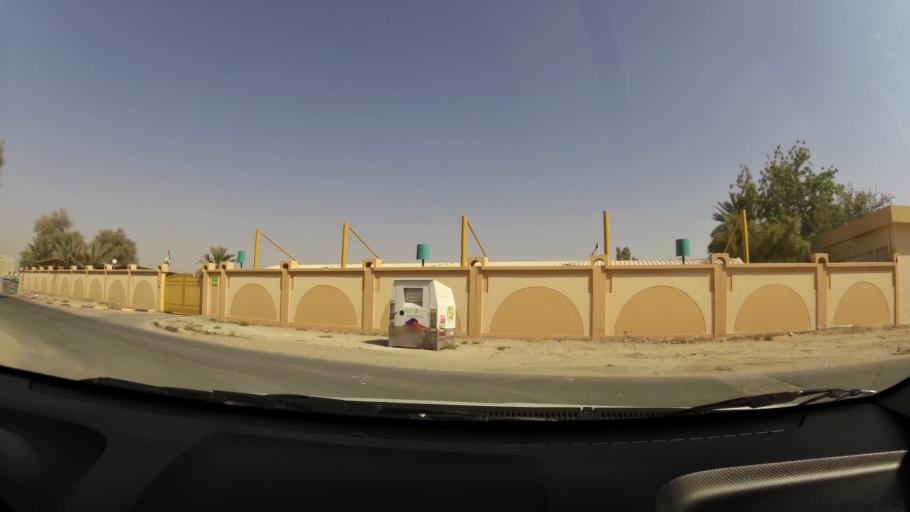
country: AE
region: Ajman
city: Ajman
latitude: 25.4136
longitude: 55.4682
